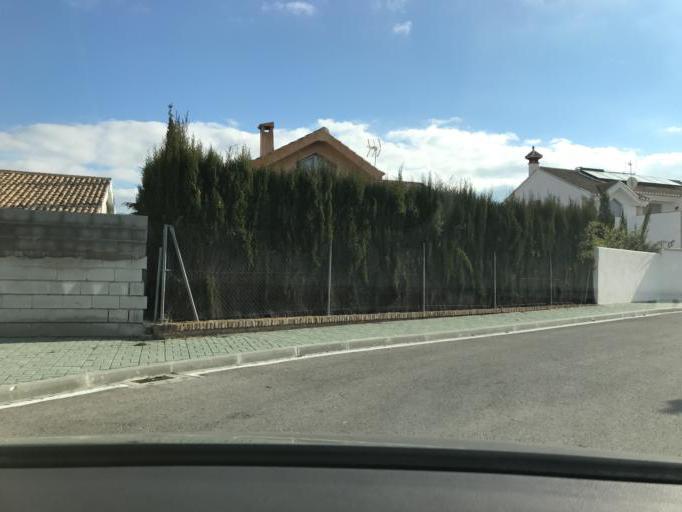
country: ES
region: Andalusia
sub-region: Provincia de Granada
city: Otura
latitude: 37.0812
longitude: -3.6239
